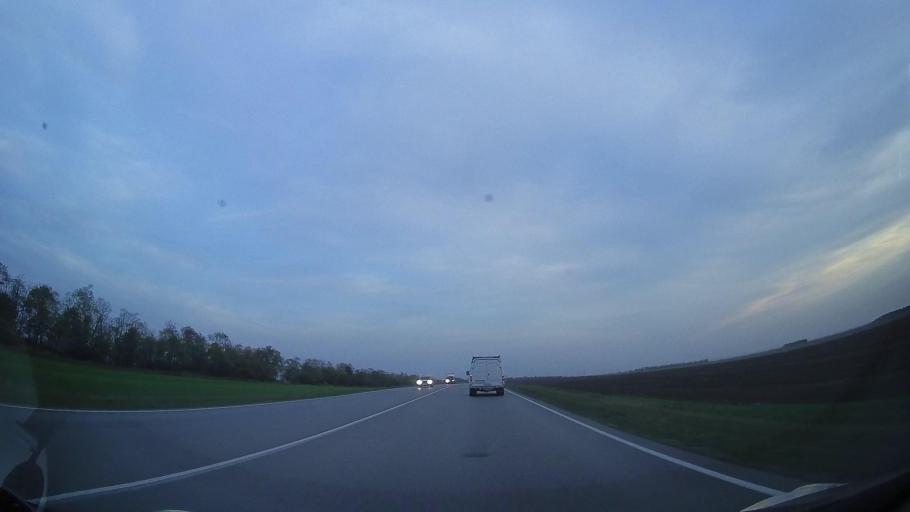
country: RU
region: Rostov
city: Kagal'nitskaya
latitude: 46.9027
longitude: 40.1212
